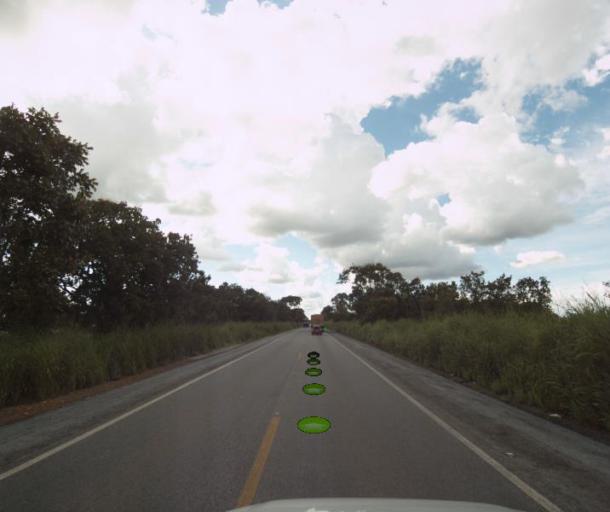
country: BR
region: Goias
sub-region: Porangatu
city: Porangatu
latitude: -13.1953
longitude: -49.1604
